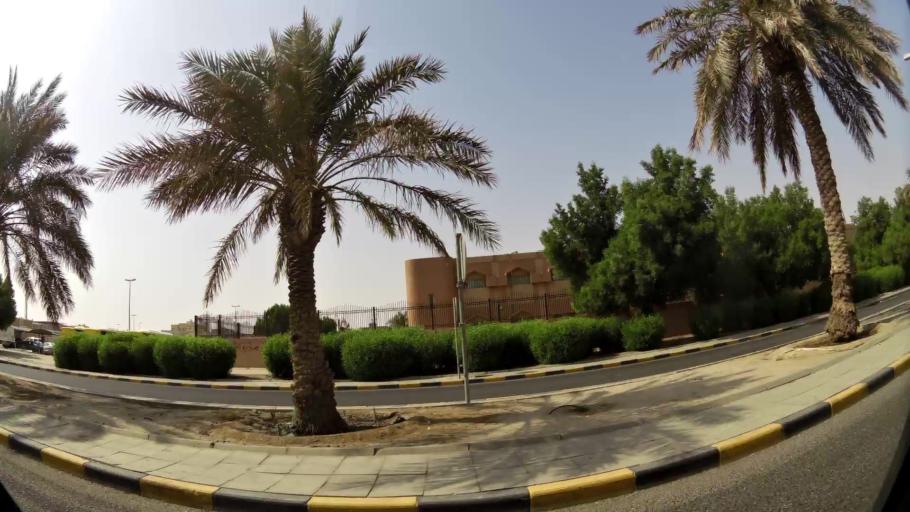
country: KW
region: Muhafazat al Jahra'
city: Al Jahra'
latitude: 29.3213
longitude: 47.6711
